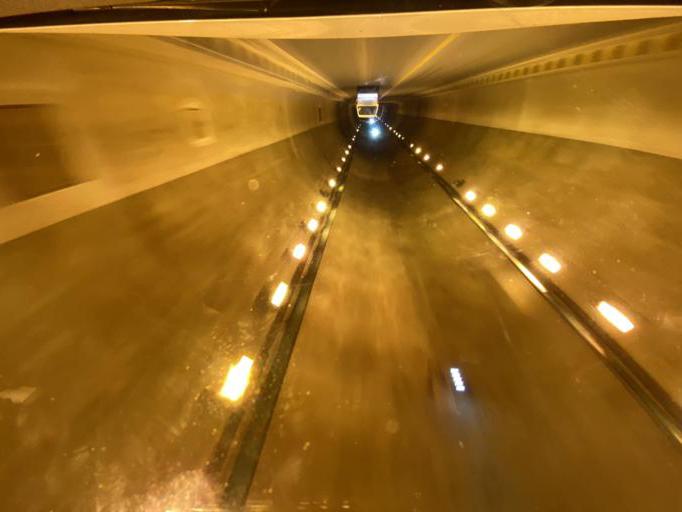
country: CN
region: Hainan
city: Tiandu
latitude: 18.3108
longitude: 109.5906
